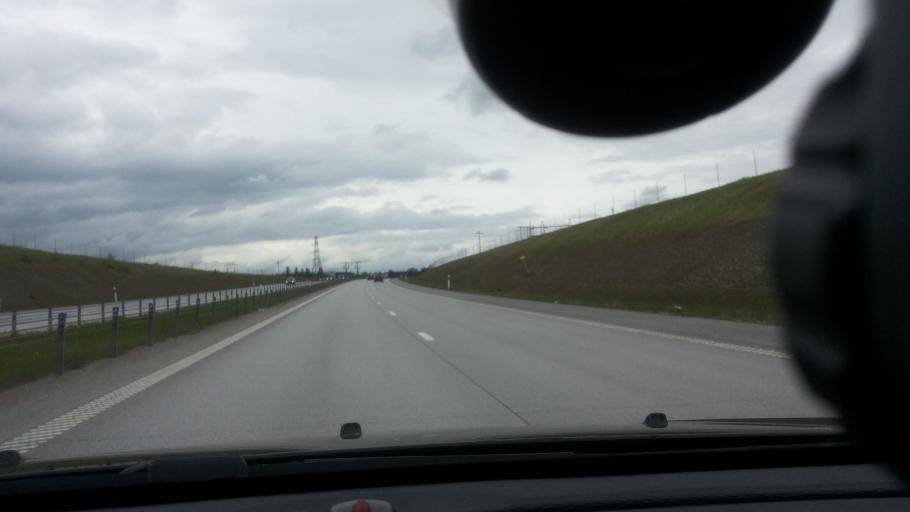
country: SE
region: Uppsala
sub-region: Uppsala Kommun
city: Gamla Uppsala
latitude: 59.9091
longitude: 17.6503
